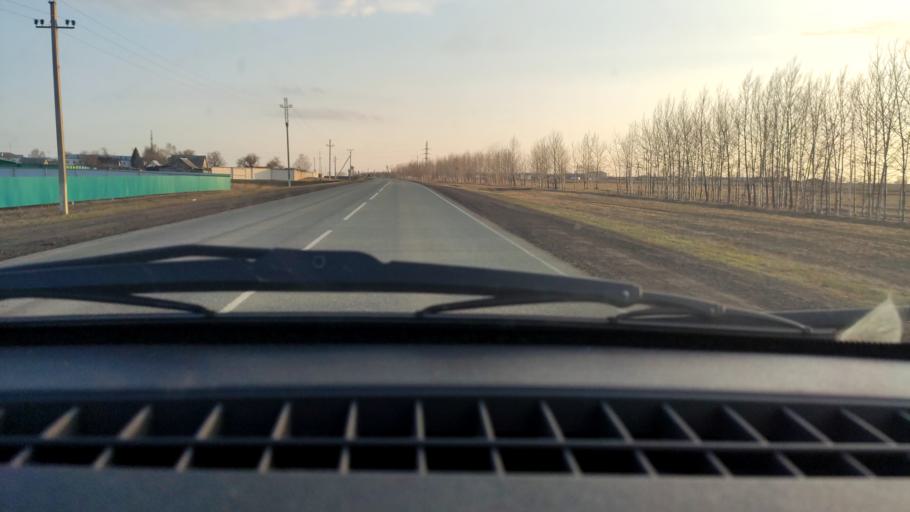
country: RU
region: Bashkortostan
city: Davlekanovo
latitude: 54.3873
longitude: 55.1996
